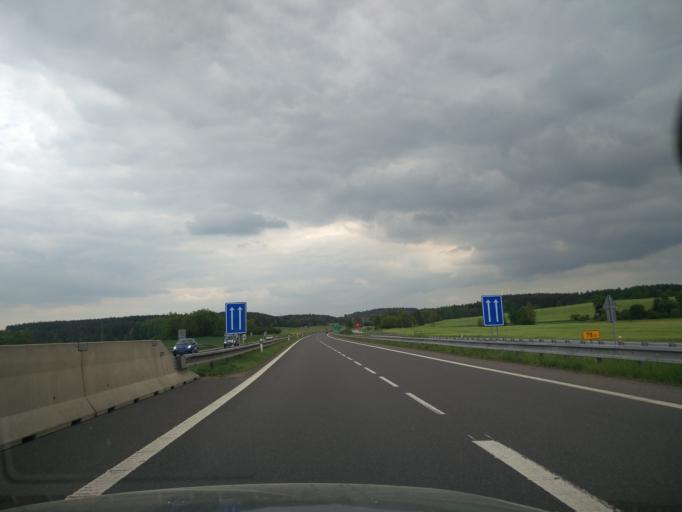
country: CZ
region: Jihocesky
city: Mirotice
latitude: 49.4120
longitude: 14.0380
